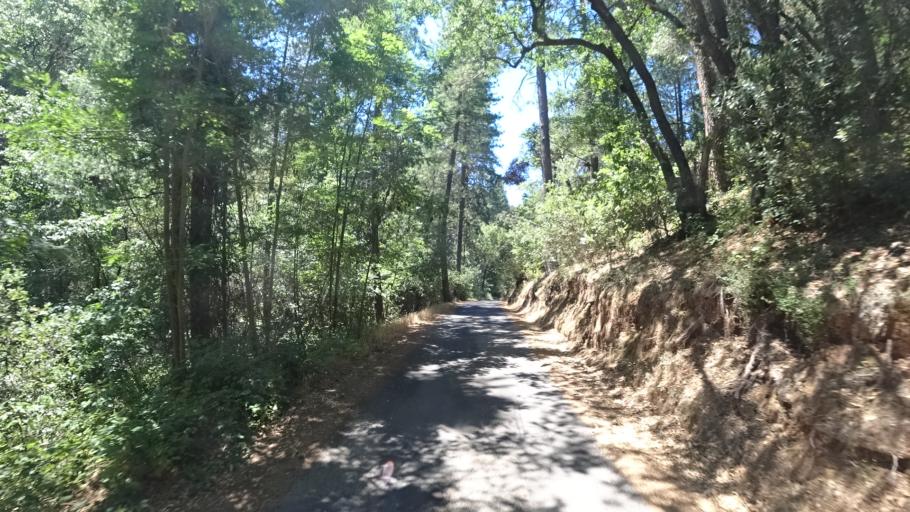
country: US
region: California
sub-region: Calaveras County
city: Forest Meadows
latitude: 38.1395
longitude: -120.4209
